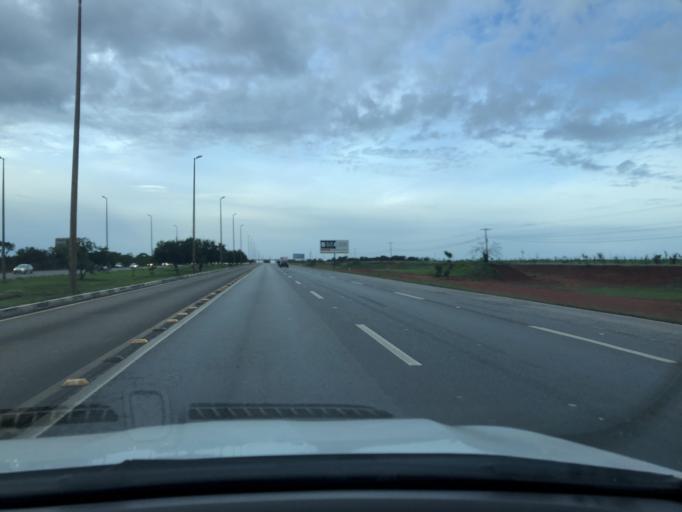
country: BR
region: Federal District
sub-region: Brasilia
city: Brasilia
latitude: -15.9634
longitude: -47.9927
